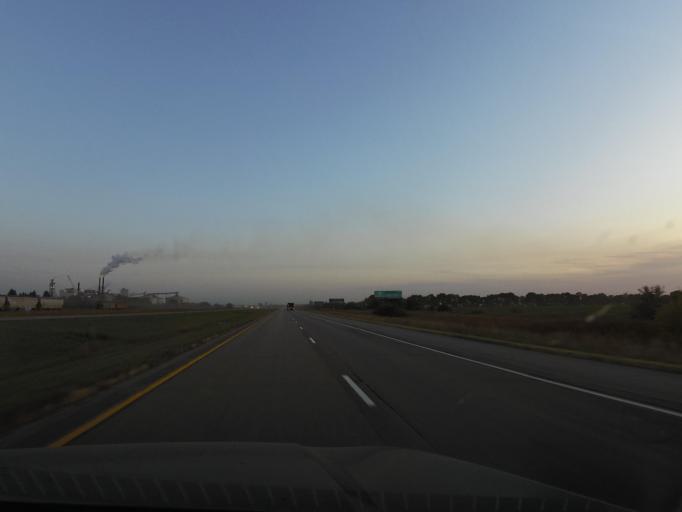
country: US
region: Minnesota
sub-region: Kittson County
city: Hallock
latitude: 48.6008
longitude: -97.1804
